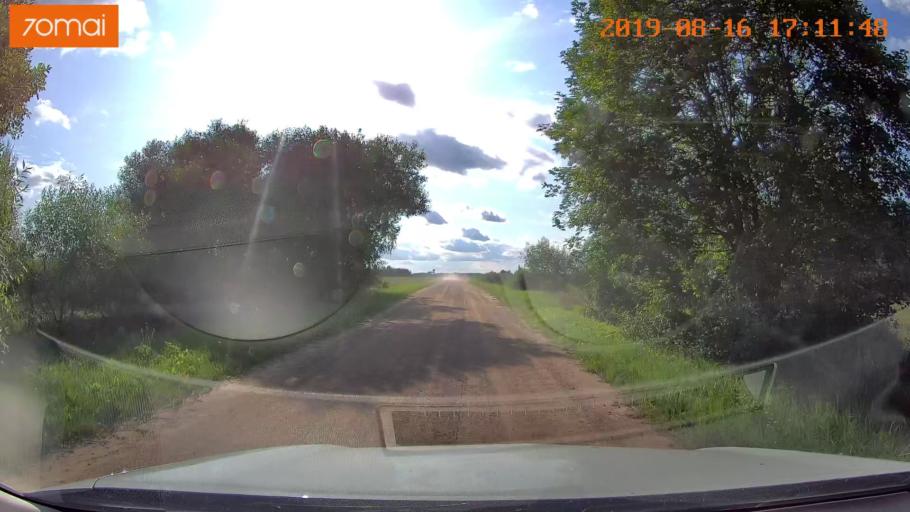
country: BY
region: Mogilev
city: Hlusha
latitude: 53.1966
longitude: 28.9010
